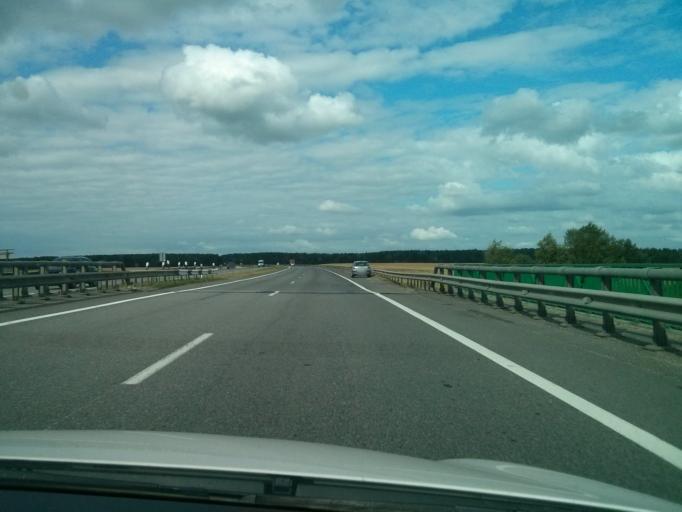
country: BY
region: Minsk
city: Zamostochcha
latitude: 53.8792
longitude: 27.9333
